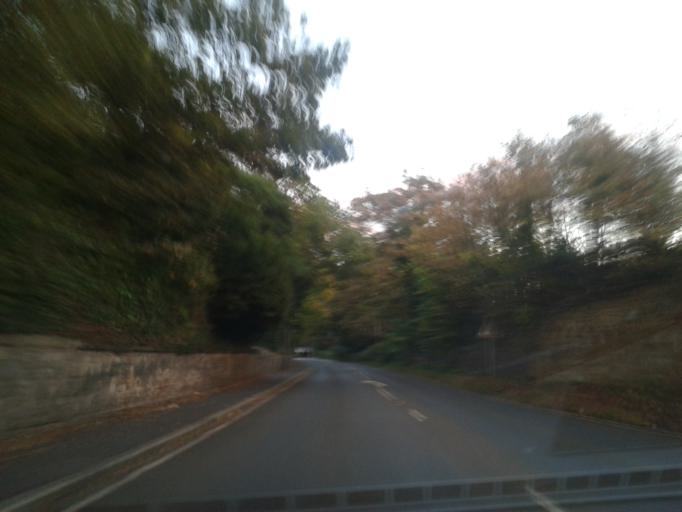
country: GB
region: Scotland
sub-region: Fife
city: Burntisland
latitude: 56.0646
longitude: -3.2075
